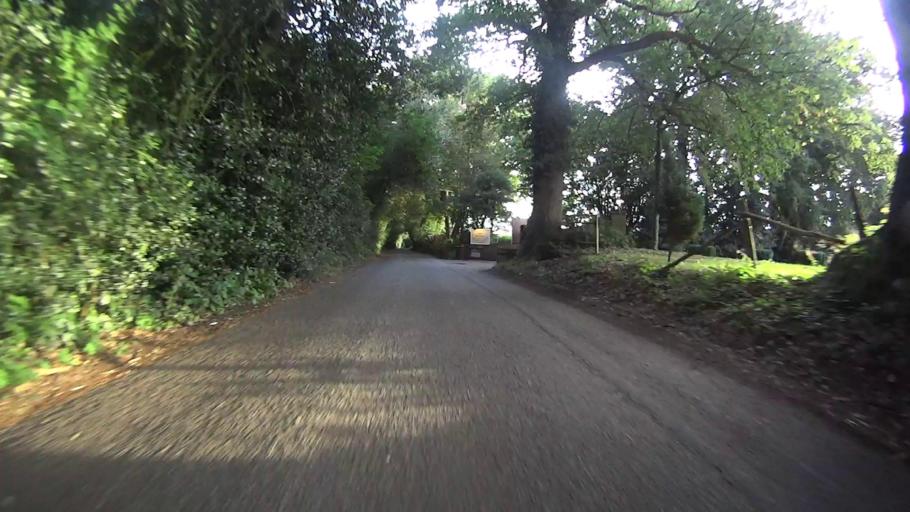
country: GB
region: England
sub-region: West Sussex
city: Copthorne
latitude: 51.1253
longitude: -0.1304
